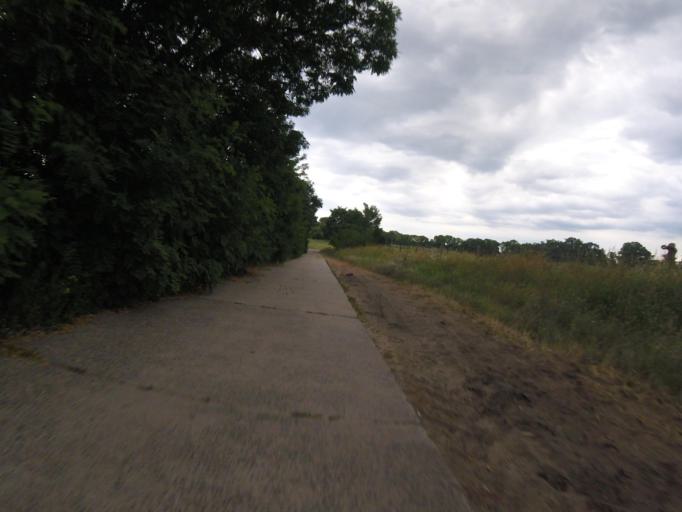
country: DE
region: Brandenburg
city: Mittenwalde
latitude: 52.2741
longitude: 13.5169
